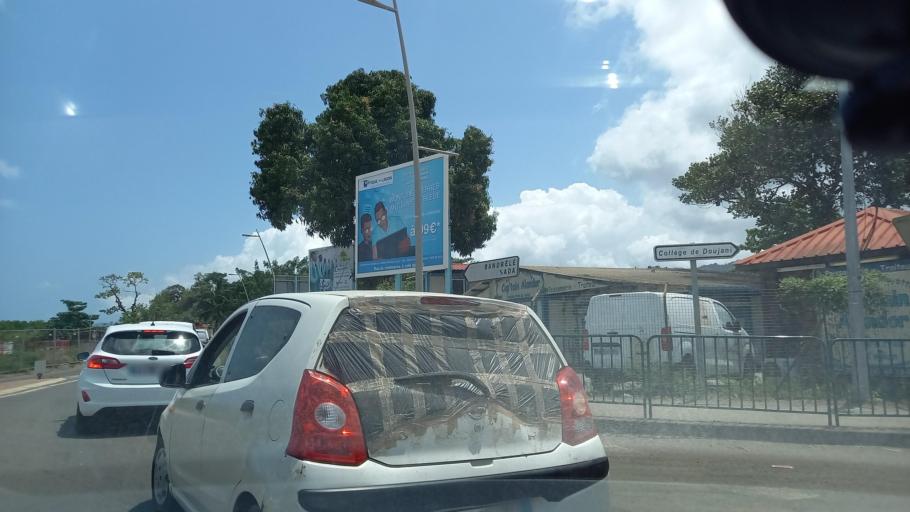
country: YT
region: Mamoudzou
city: Mamoudzou
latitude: -12.7944
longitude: 45.2165
